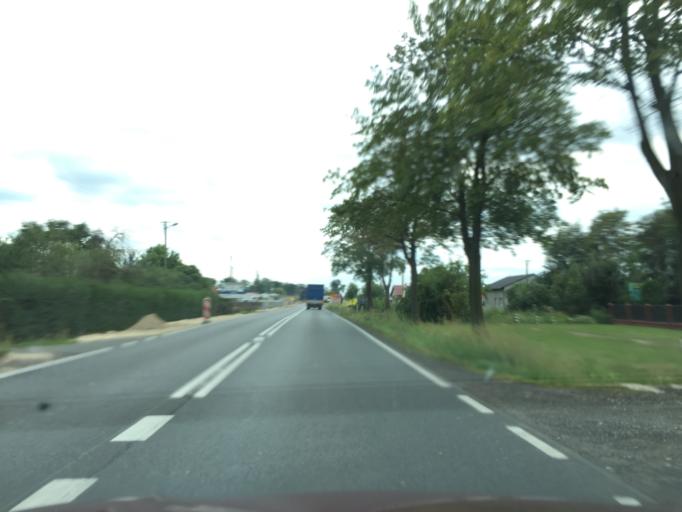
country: PL
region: Greater Poland Voivodeship
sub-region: Kalisz
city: Kalisz
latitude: 51.8012
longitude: 18.0922
